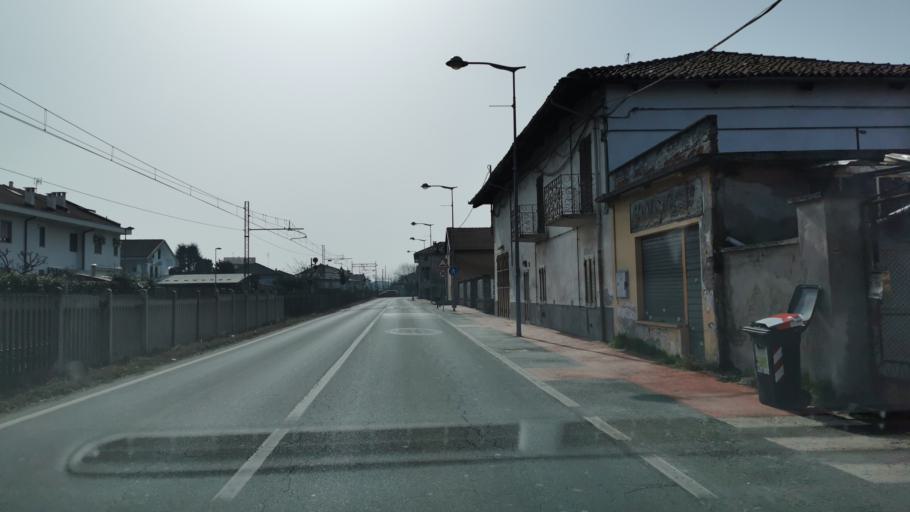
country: IT
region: Piedmont
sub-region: Provincia di Torino
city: Volpiano
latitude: 45.2063
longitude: 7.7803
